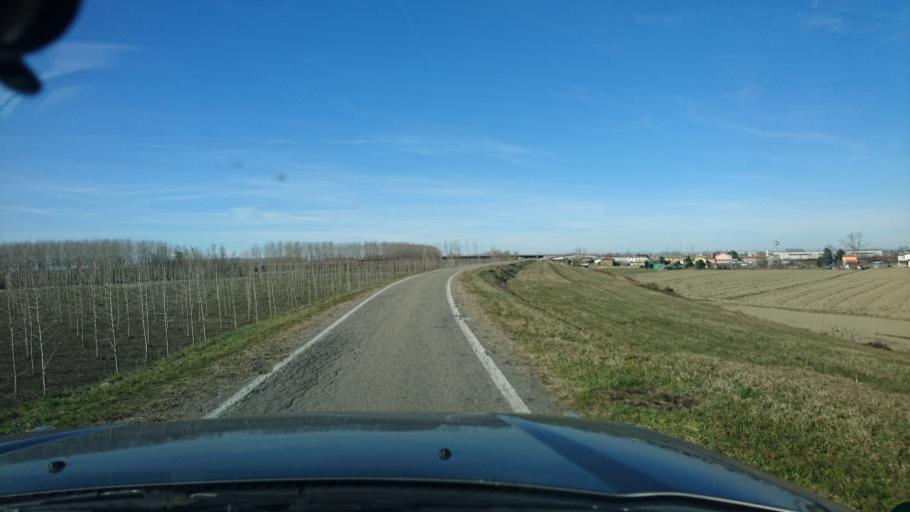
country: IT
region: Veneto
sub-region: Provincia di Rovigo
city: Ariano
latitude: 44.9349
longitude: 12.1310
